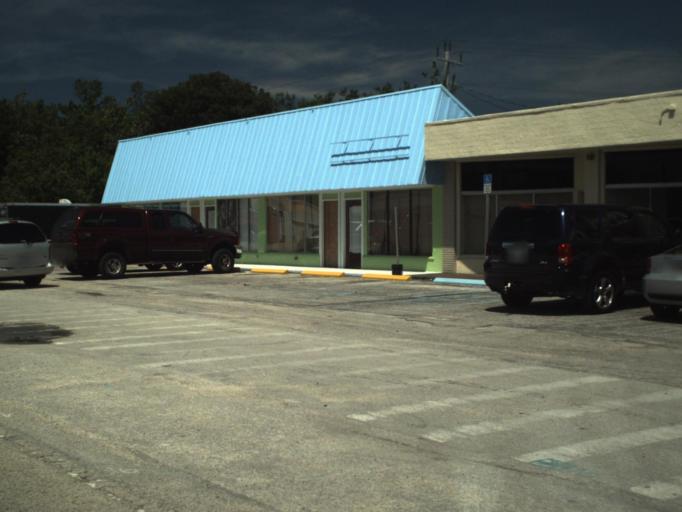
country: US
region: Florida
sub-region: Monroe County
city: Marathon
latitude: 24.7104
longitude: -81.0976
